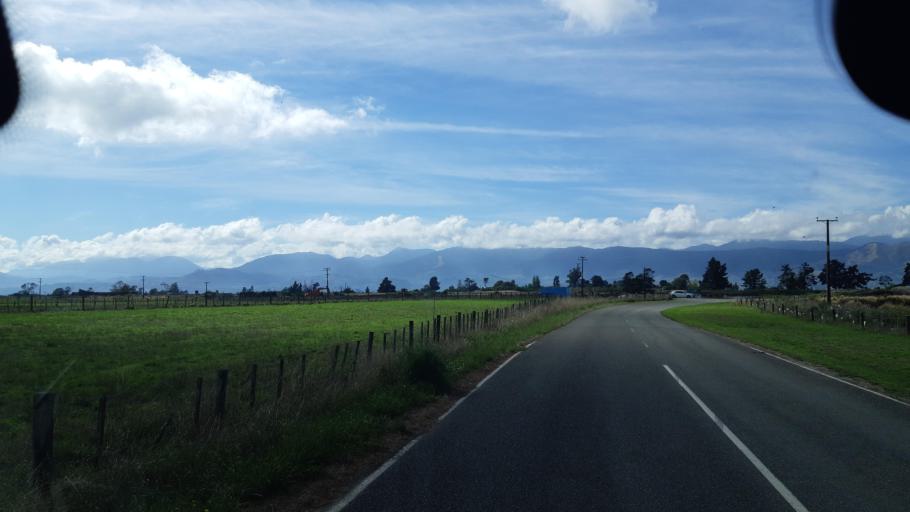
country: NZ
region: Tasman
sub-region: Tasman District
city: Richmond
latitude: -41.2952
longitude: 173.1526
